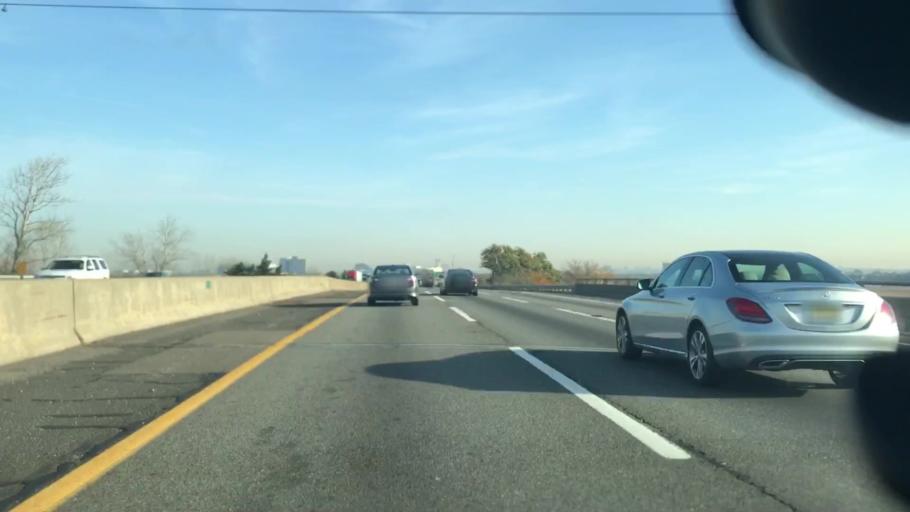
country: US
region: New Jersey
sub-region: Bergen County
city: North Arlington
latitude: 40.7827
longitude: -74.0955
